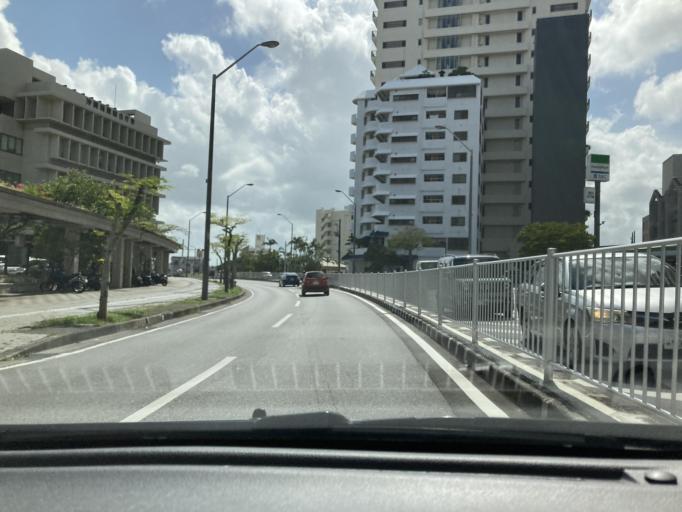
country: JP
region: Okinawa
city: Naha-shi
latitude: 26.2253
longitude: 127.6930
